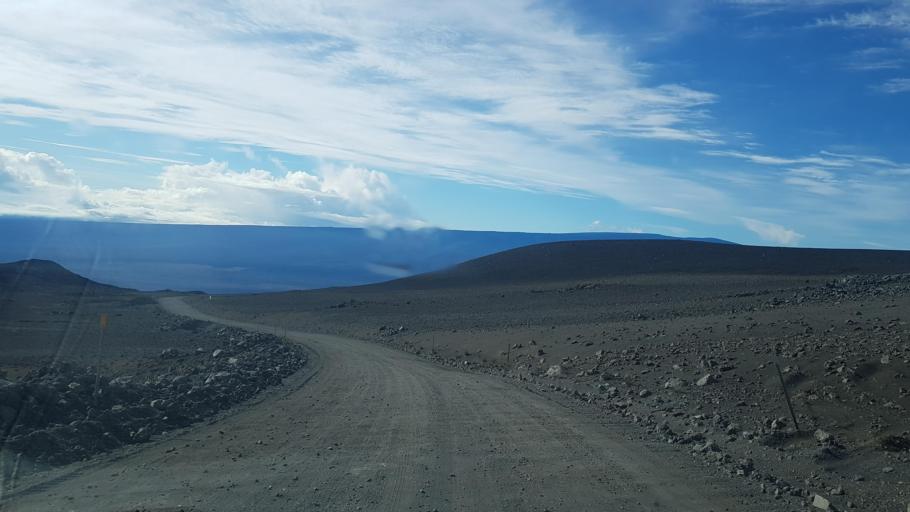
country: US
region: Hawaii
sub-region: Hawaii County
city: Honoka'a
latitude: 19.7863
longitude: -155.4546
